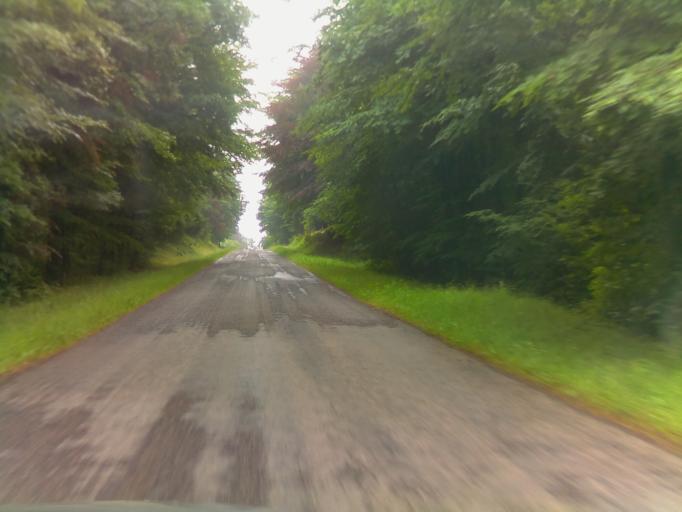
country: BE
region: Wallonia
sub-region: Province du Luxembourg
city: Leglise
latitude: 49.7685
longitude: 5.5804
